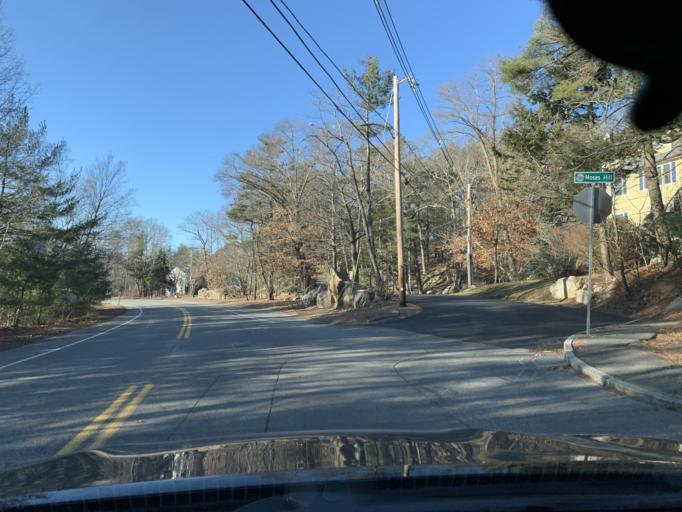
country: US
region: Massachusetts
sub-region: Essex County
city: Essex
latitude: 42.5879
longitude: -70.7841
